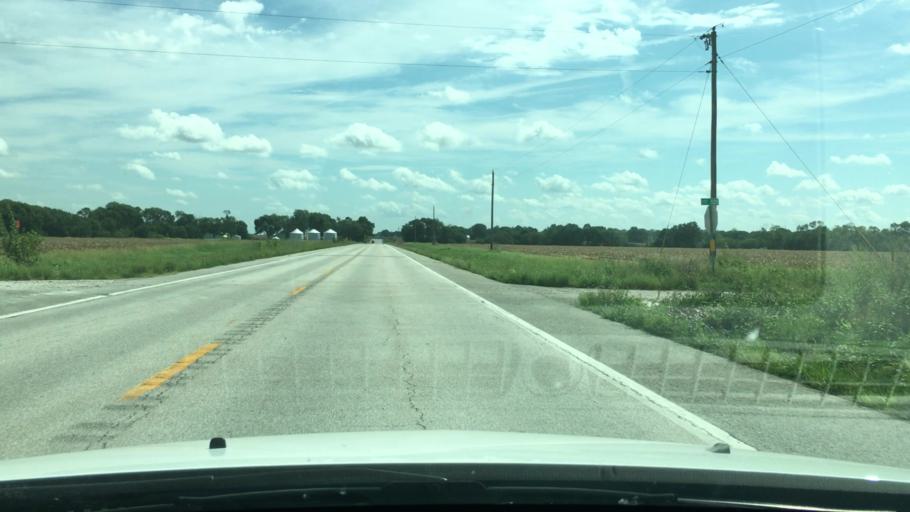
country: US
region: Missouri
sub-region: Audrain County
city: Vandalia
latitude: 39.2796
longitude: -91.5908
